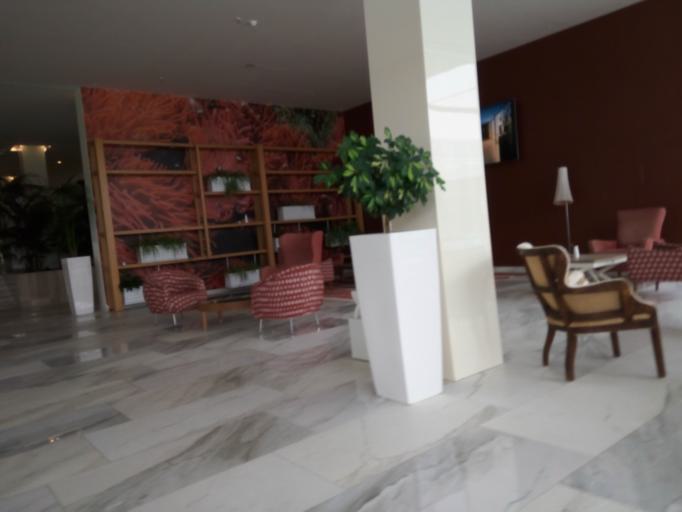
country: HR
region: Sibensko-Kniniska
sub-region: Grad Sibenik
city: Sibenik
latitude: 43.6955
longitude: 15.8844
